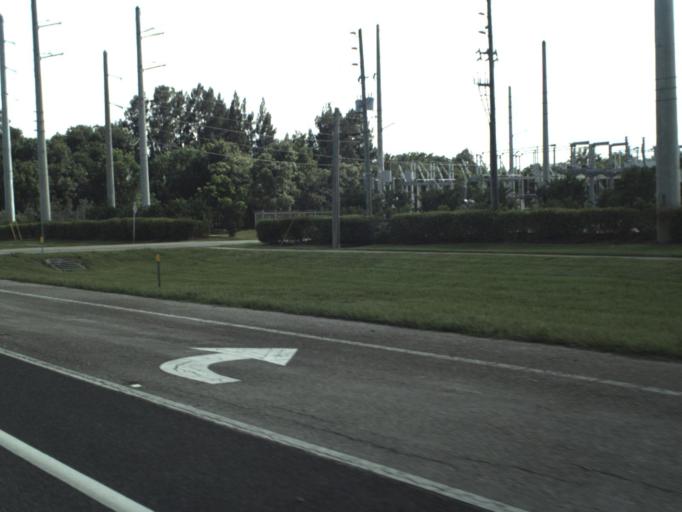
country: US
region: Florida
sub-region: Palm Beach County
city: Villages of Oriole
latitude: 26.4289
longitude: -80.2044
